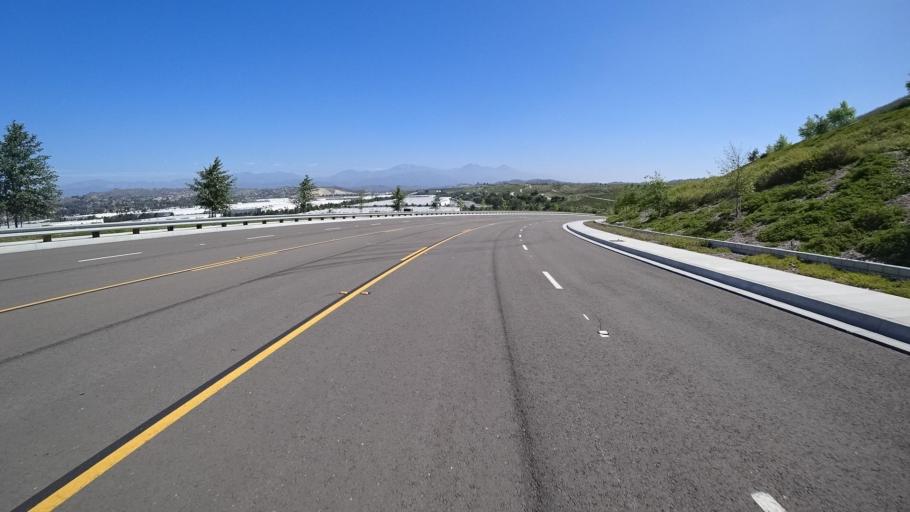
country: US
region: California
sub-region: Los Angeles County
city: Walnut
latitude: 34.0060
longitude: -117.8387
